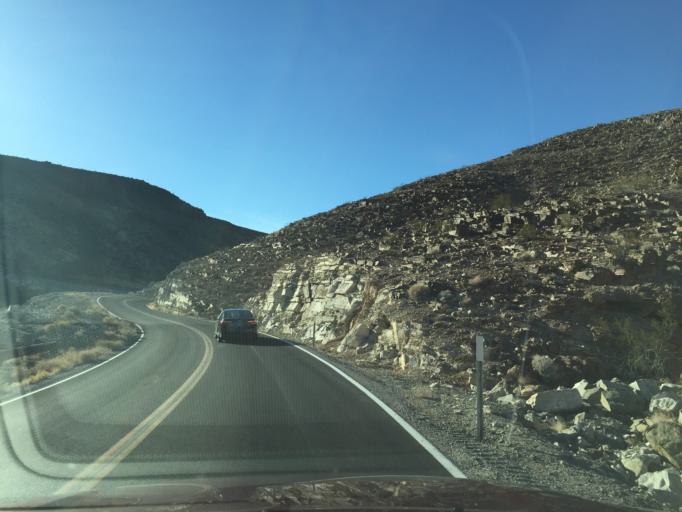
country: US
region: California
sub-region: Inyo County
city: Lone Pine
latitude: 36.3484
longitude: -117.5380
